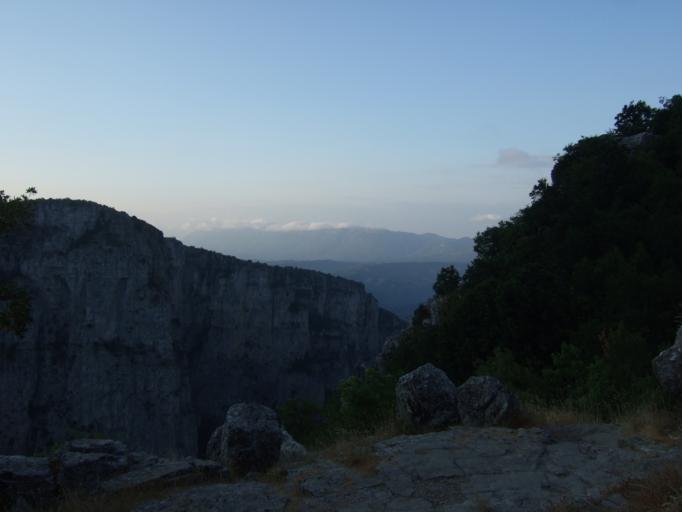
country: GR
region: Epirus
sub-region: Nomos Ioanninon
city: Asprangeloi
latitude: 39.9066
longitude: 20.7518
